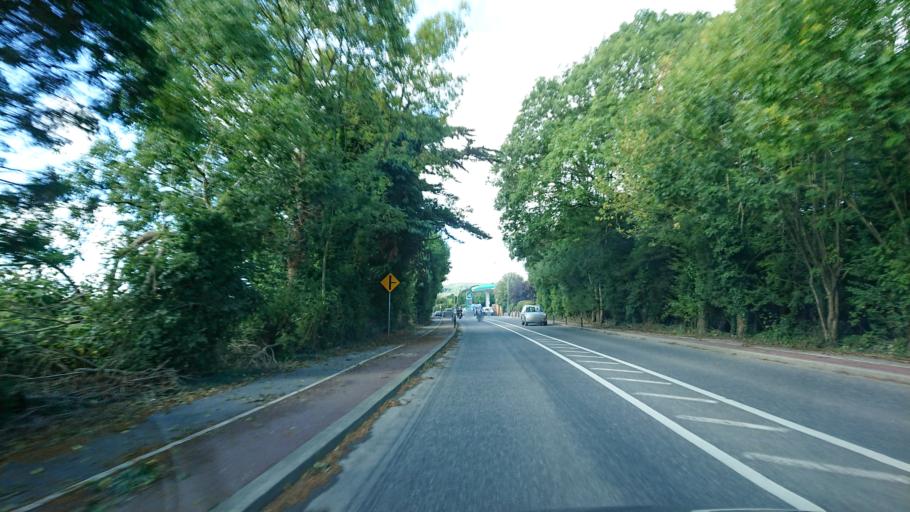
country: IE
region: Munster
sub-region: Waterford
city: Dungarvan
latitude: 52.1077
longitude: -7.6659
